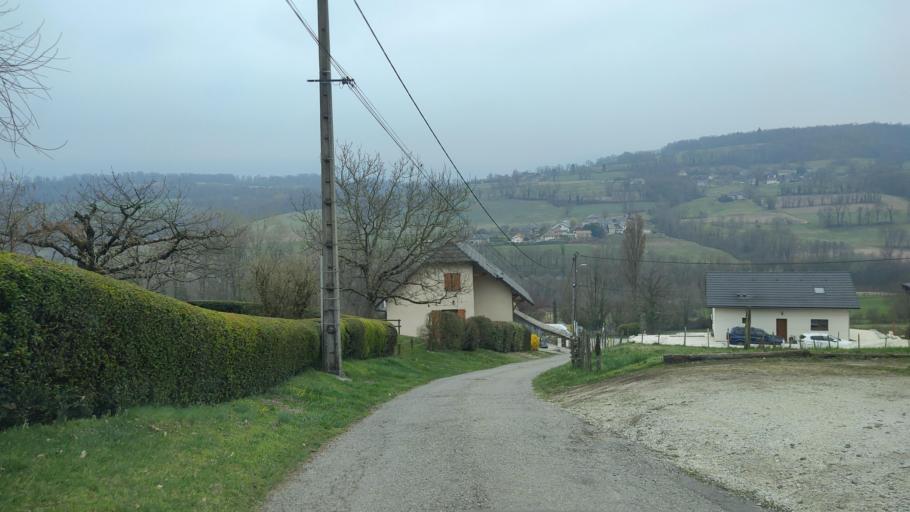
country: FR
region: Rhone-Alpes
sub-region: Departement de la Savoie
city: La Biolle
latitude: 45.7578
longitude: 5.9400
